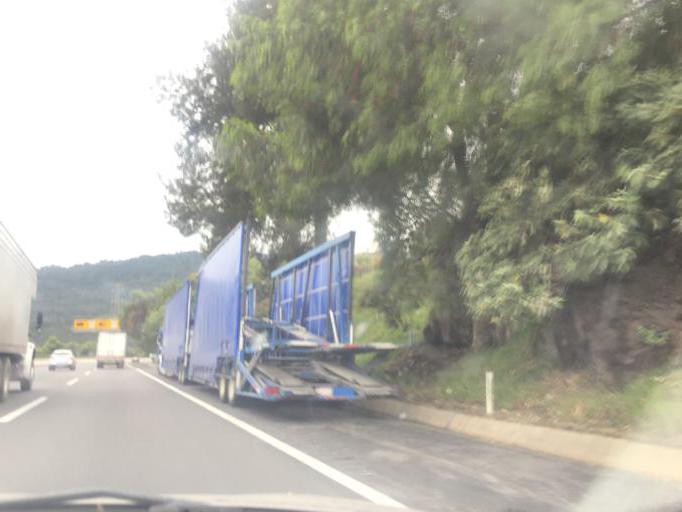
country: MX
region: Mexico City
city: Xochimilco
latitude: 19.2347
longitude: -99.1447
